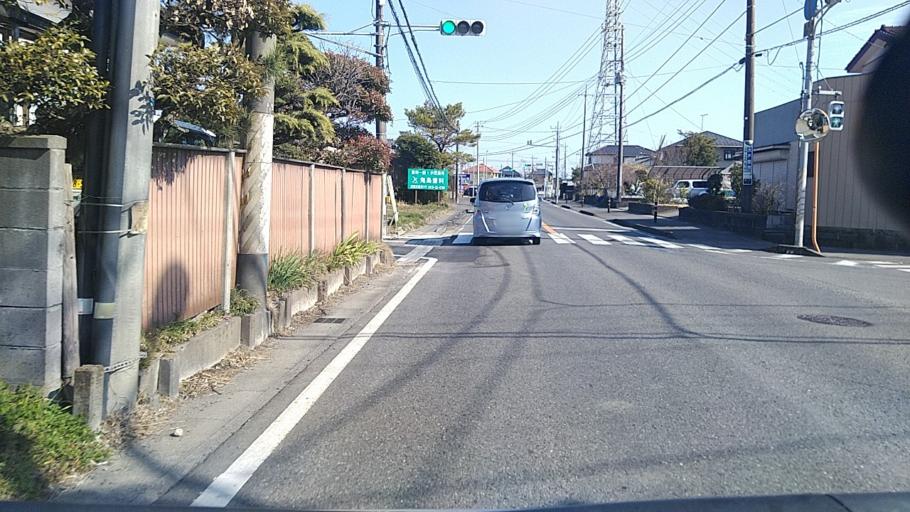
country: JP
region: Chiba
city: Mobara
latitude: 35.4251
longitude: 140.2787
